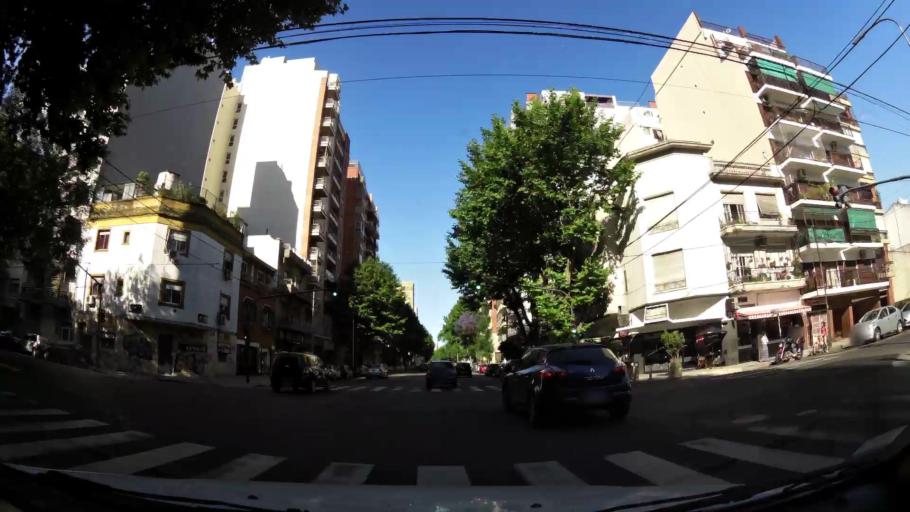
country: AR
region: Buenos Aires F.D.
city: Villa Santa Rita
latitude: -34.6212
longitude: -58.4562
